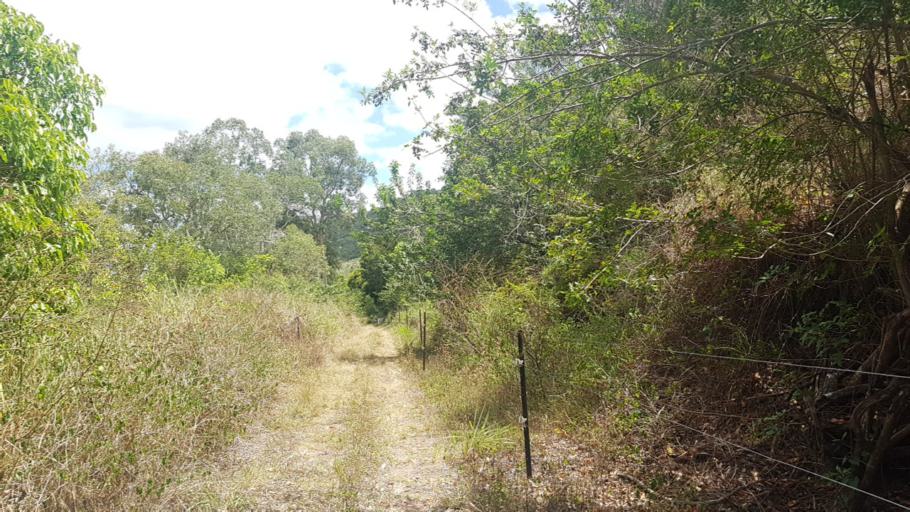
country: NC
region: South Province
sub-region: Dumbea
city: Dumbea
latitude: -22.1739
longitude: 166.4706
